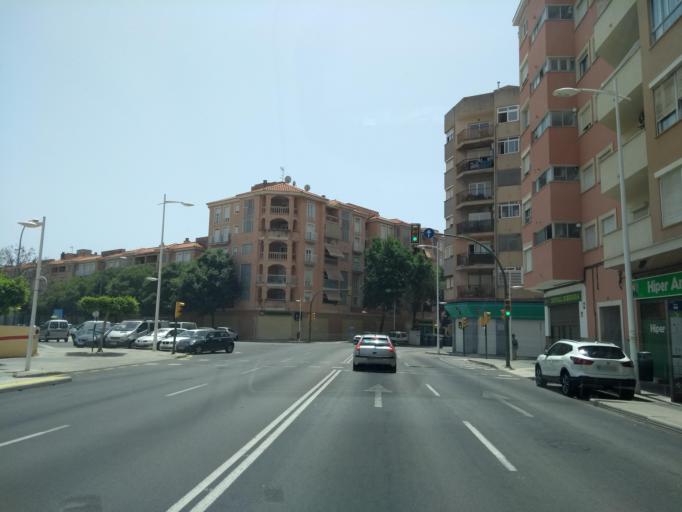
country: ES
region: Balearic Islands
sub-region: Illes Balears
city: Palma
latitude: 39.5850
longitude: 2.6625
